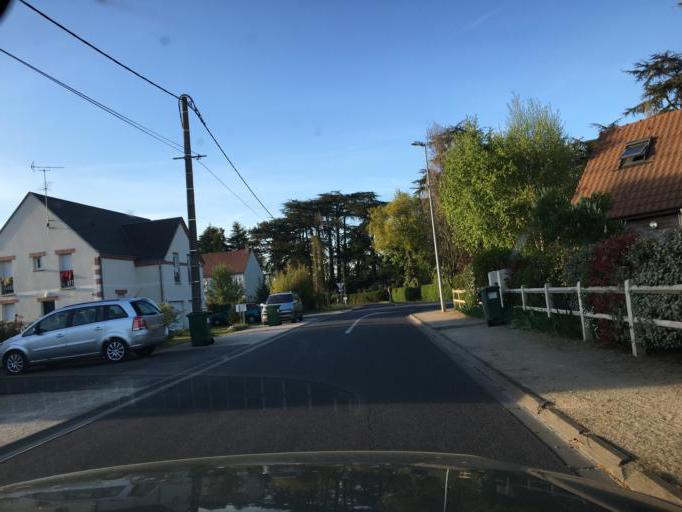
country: FR
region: Centre
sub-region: Departement du Loiret
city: Saint-Denis-en-Val
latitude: 47.8830
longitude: 1.9523
